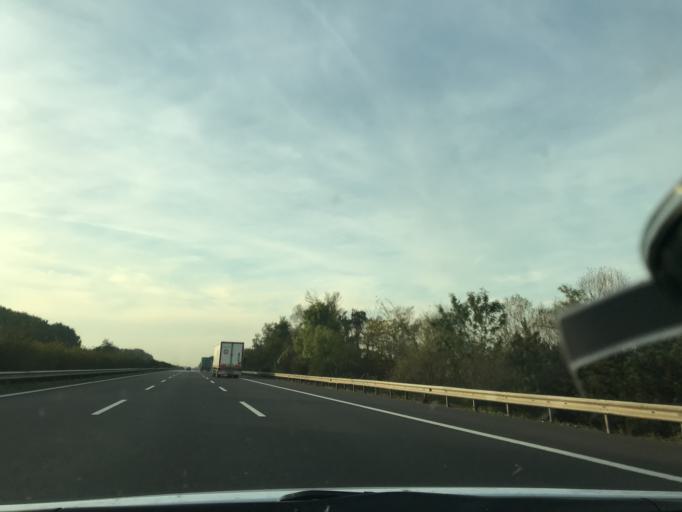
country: TR
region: Duzce
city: Cilimli
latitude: 40.8200
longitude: 31.0721
